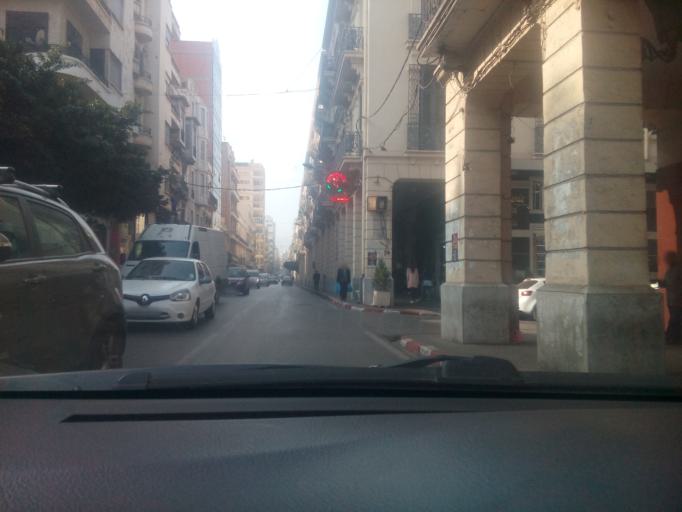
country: DZ
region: Oran
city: Oran
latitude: 35.7028
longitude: -0.6377
